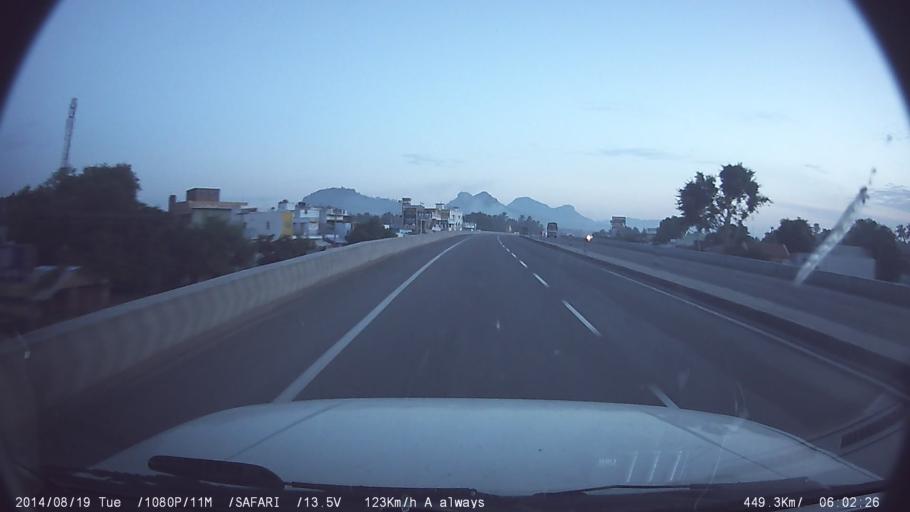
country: IN
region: Tamil Nadu
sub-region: Salem
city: Omalur
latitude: 11.8373
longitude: 78.0665
